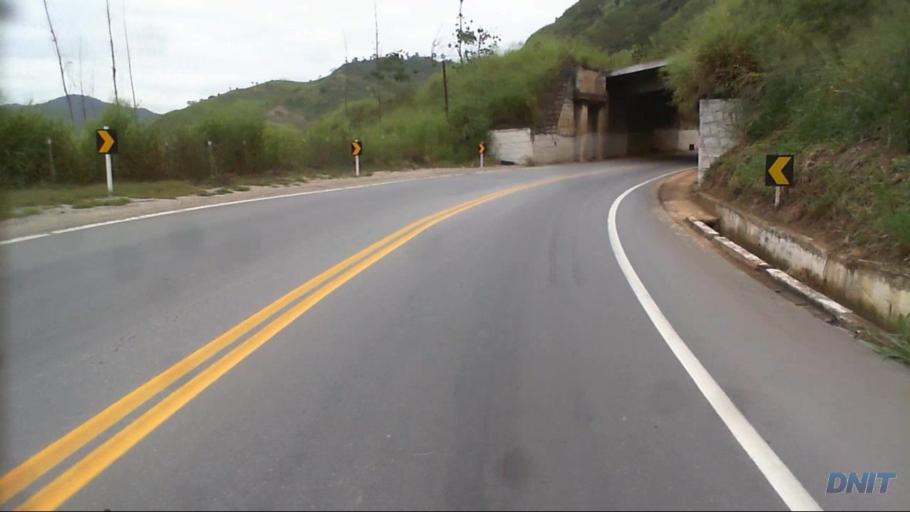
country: BR
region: Minas Gerais
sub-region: Timoteo
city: Timoteo
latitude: -19.6388
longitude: -42.8094
